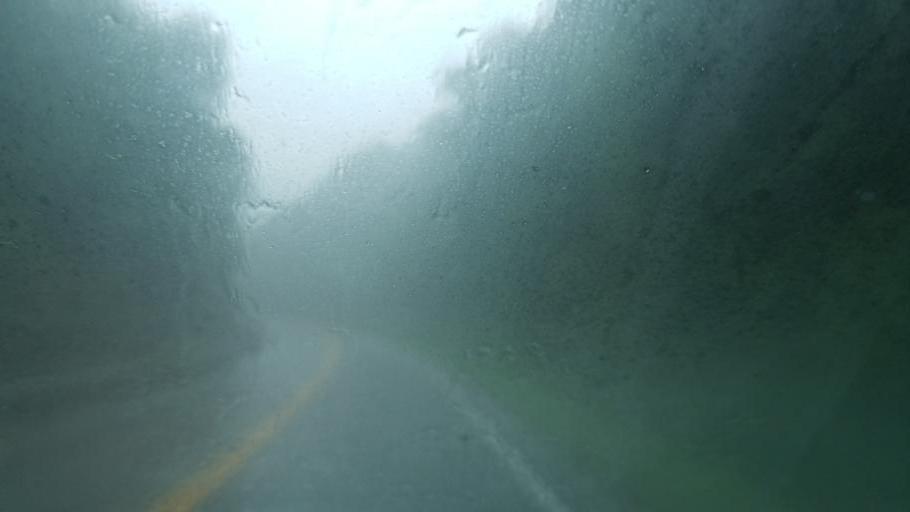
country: US
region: Kentucky
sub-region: Rowan County
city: Morehead
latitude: 38.2590
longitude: -83.5312
